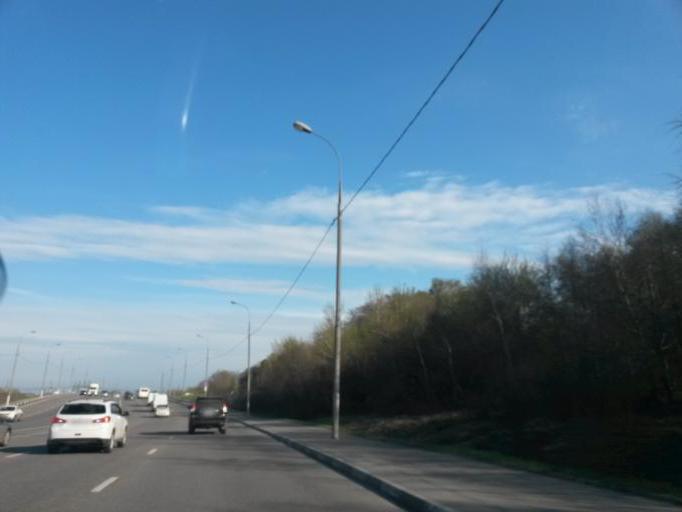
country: RU
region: Moscow
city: Zyablikovo
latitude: 55.6218
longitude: 37.7625
